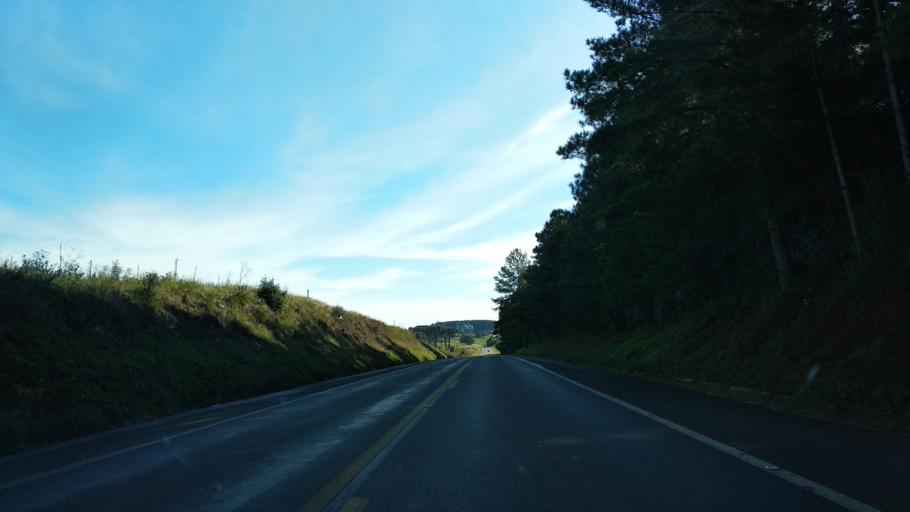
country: BR
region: Santa Catarina
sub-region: Celso Ramos
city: Celso Ramos
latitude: -27.5271
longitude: -51.3657
